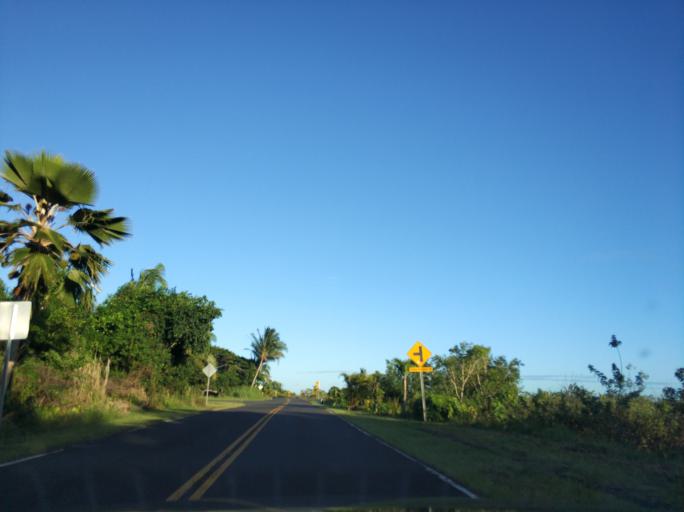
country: US
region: Hawaii
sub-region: Hawaii County
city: Leilani Estates
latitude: 19.3626
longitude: -154.9675
